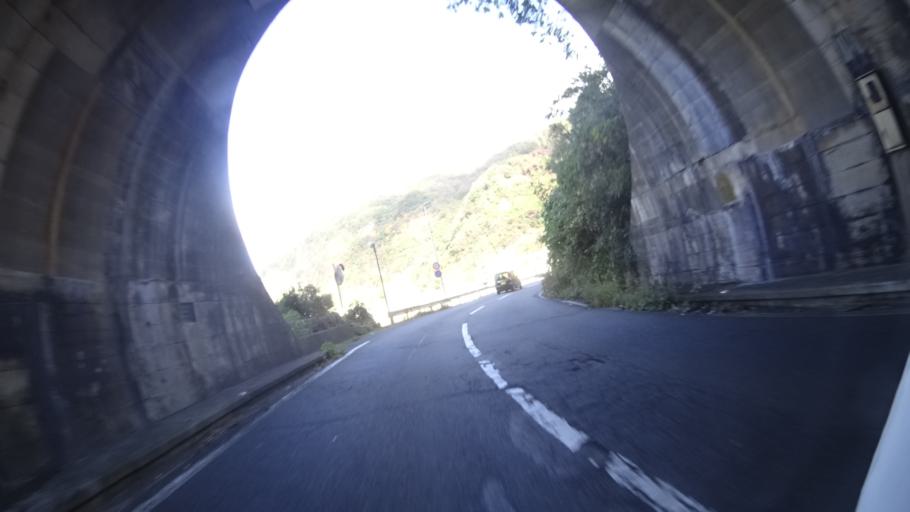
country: JP
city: Asahi
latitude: 35.9668
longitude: 135.9685
